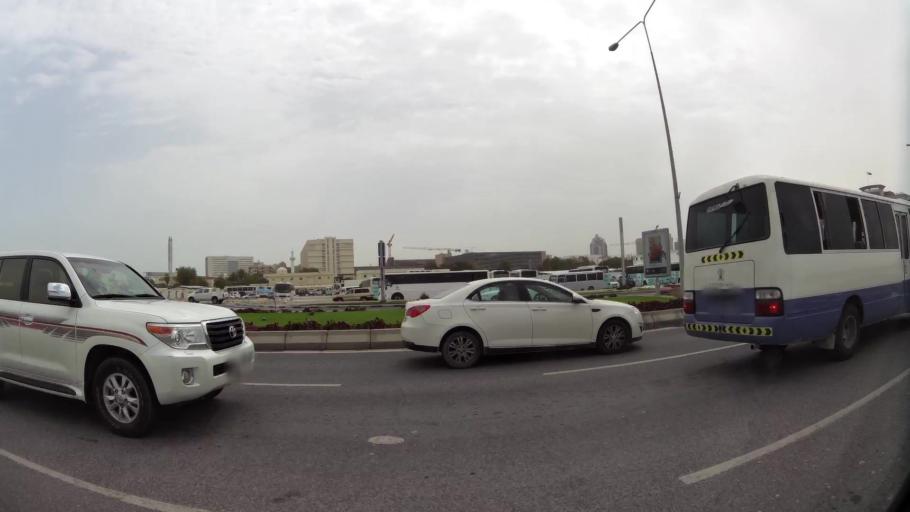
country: QA
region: Baladiyat ad Dawhah
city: Doha
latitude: 25.2941
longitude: 51.4970
